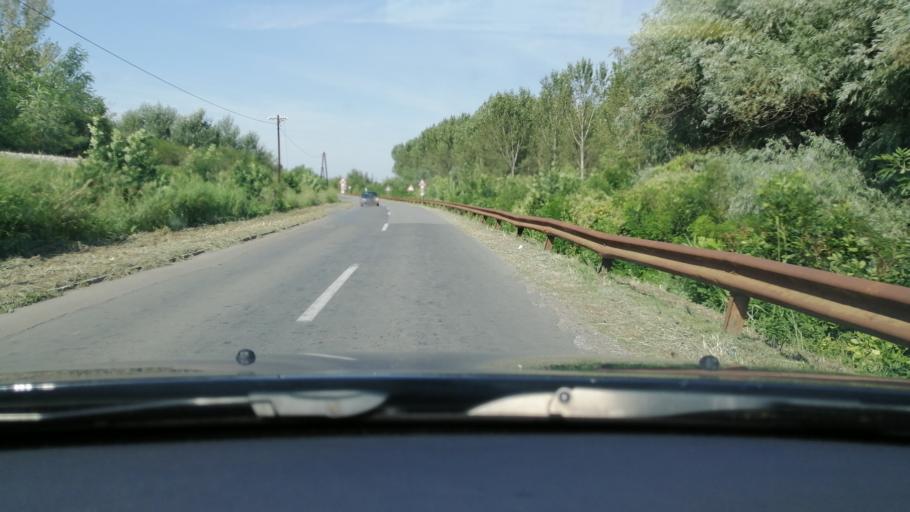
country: RS
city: Orlovat
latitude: 45.2491
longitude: 20.5992
